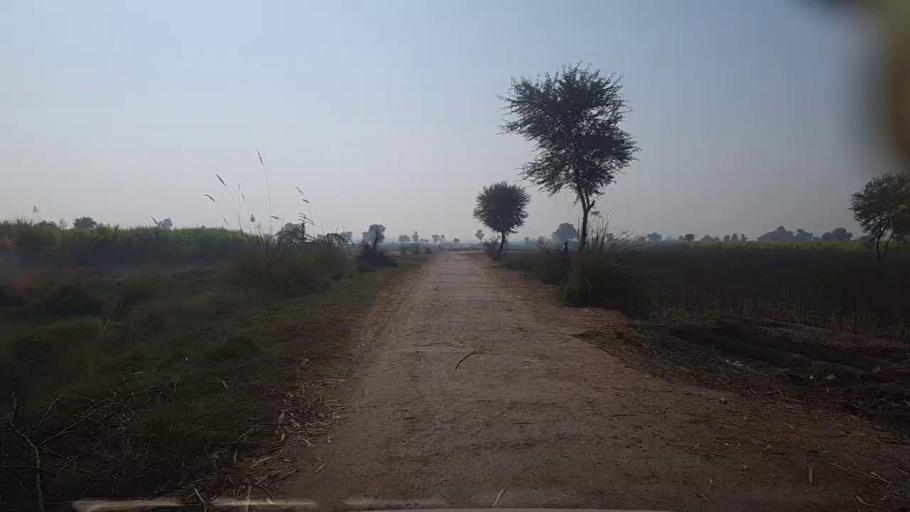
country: PK
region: Sindh
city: Kandiari
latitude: 26.9953
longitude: 68.4906
